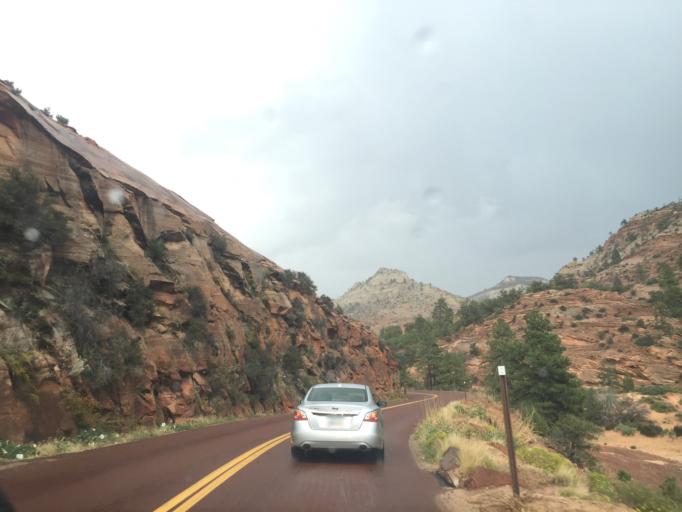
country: US
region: Utah
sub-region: Washington County
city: Hildale
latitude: 37.2186
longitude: -112.9183
